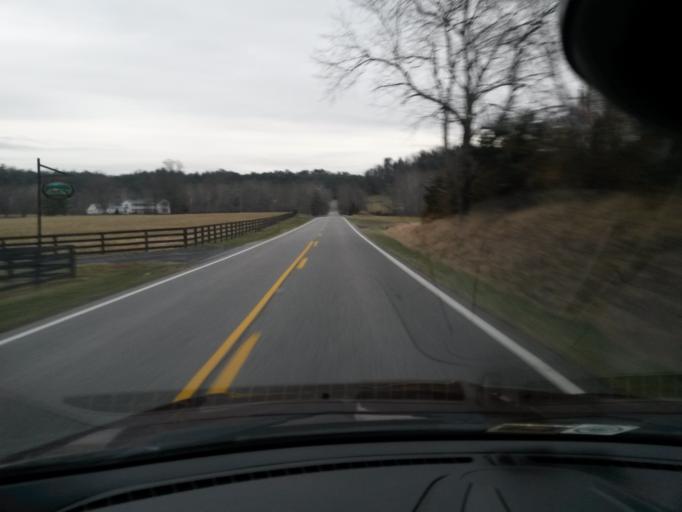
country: US
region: Virginia
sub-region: Bath County
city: Warm Springs
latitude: 38.0180
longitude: -79.6423
